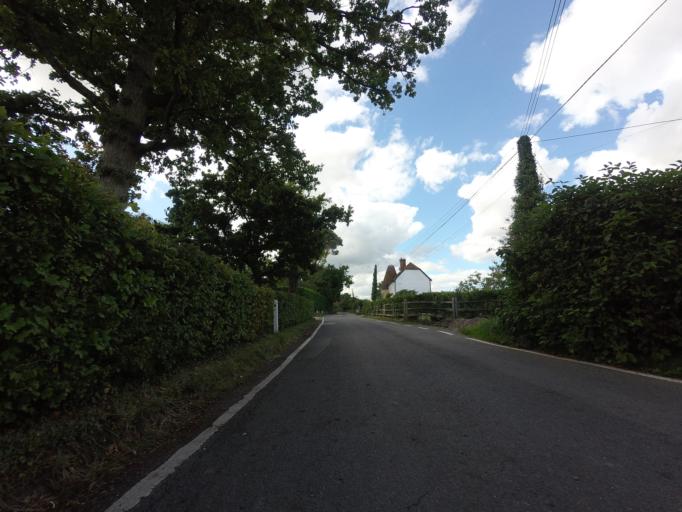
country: GB
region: England
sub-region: Kent
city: Staplehurst
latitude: 51.1535
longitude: 0.5231
